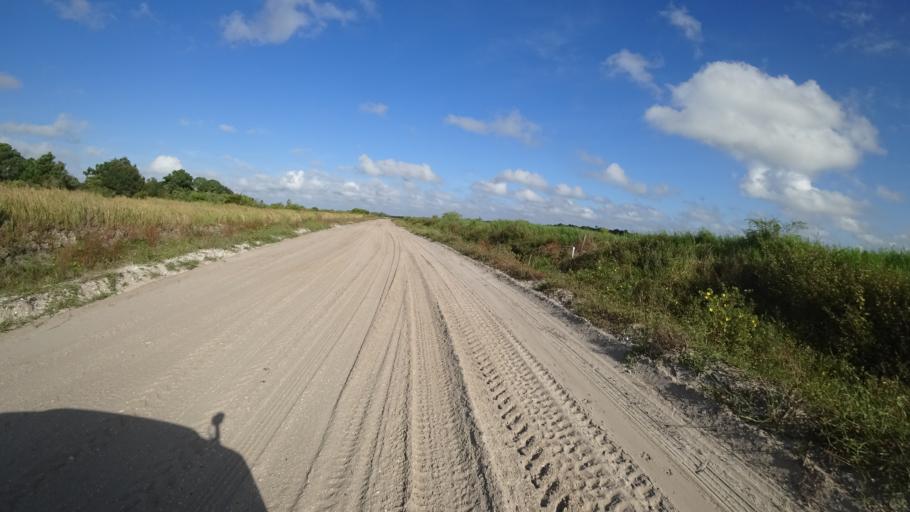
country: US
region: Florida
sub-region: Hillsborough County
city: Wimauma
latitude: 27.5517
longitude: -82.3210
